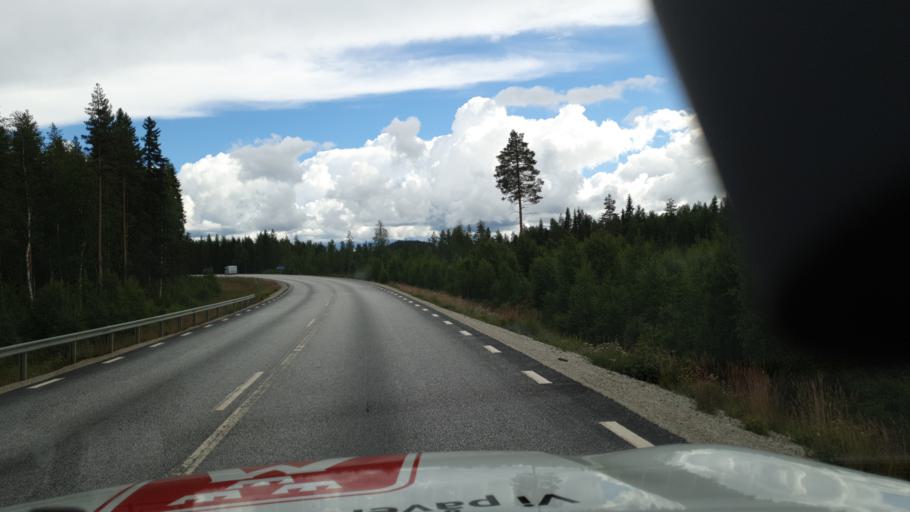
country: SE
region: Vaesterbotten
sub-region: Vindelns Kommun
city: Vindeln
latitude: 64.0566
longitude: 19.6497
